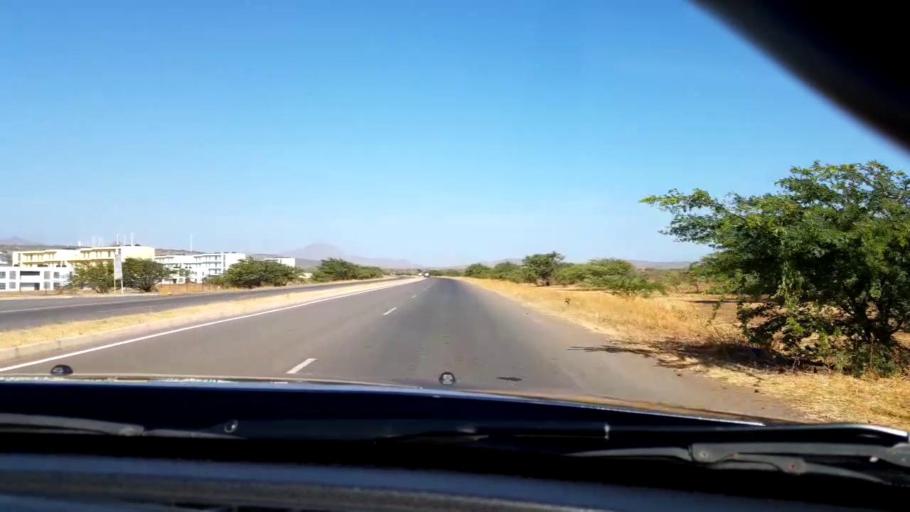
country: CV
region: Praia
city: Praia
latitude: 14.9485
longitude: -23.4908
